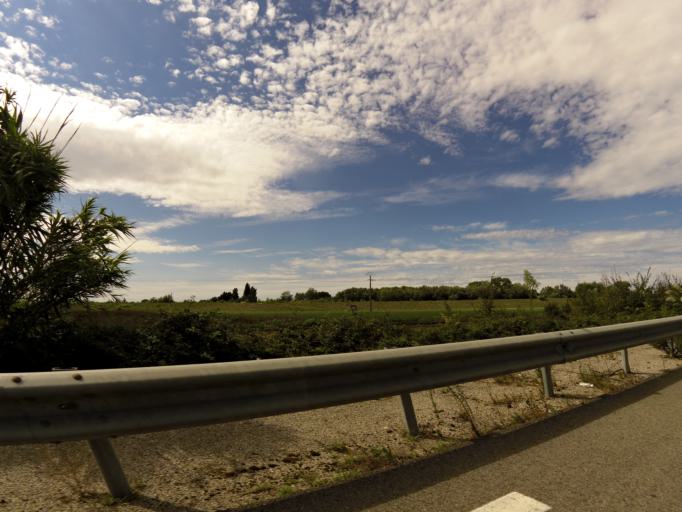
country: FR
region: Languedoc-Roussillon
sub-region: Departement de l'Herault
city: Marsillargues
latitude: 43.6329
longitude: 4.1896
